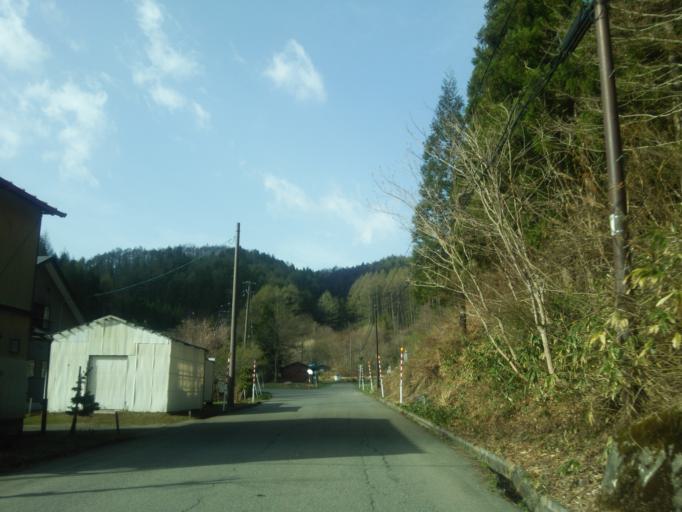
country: JP
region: Fukushima
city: Inawashiro
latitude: 37.6458
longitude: 140.1705
